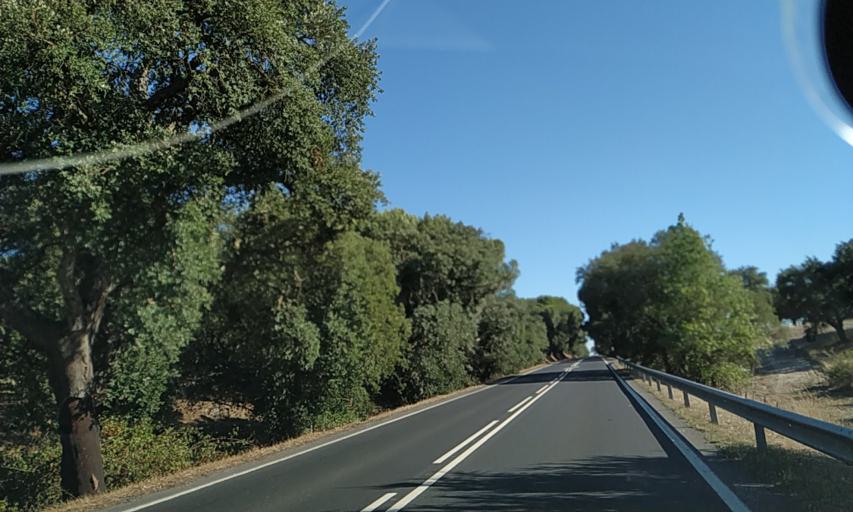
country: PT
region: Santarem
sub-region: Benavente
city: Samora Correia
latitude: 38.8962
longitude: -8.8814
